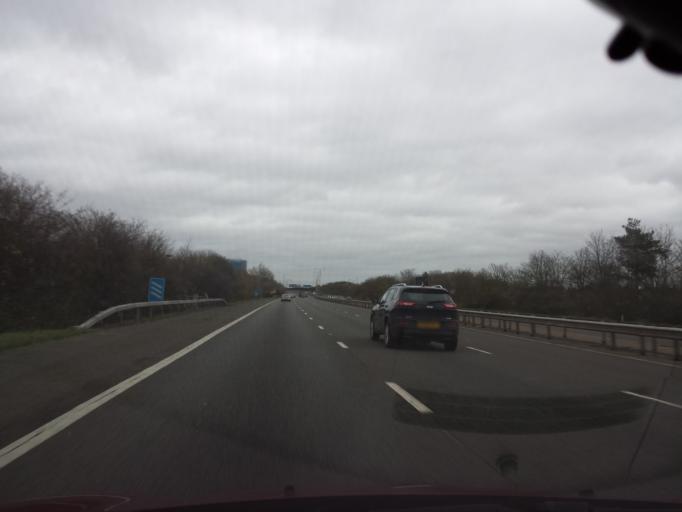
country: GB
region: England
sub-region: Surrey
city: Sunbury-on-Thames
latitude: 51.4145
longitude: -0.4295
